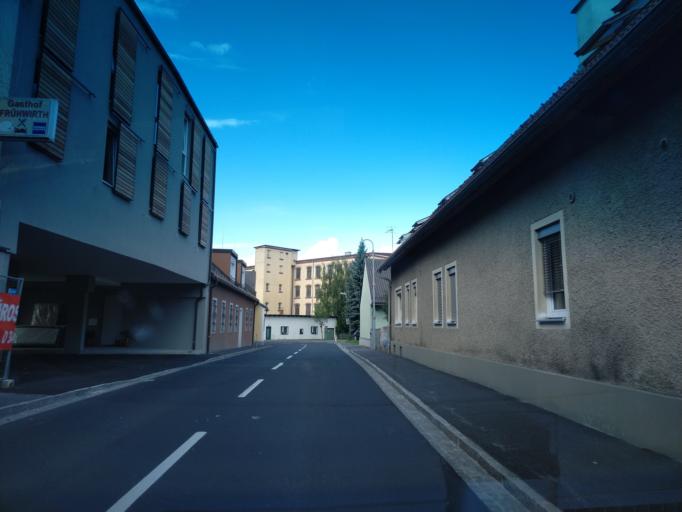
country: AT
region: Styria
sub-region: Politischer Bezirk Leibnitz
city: Kaindorf an der Sulm
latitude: 46.7922
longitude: 15.5332
